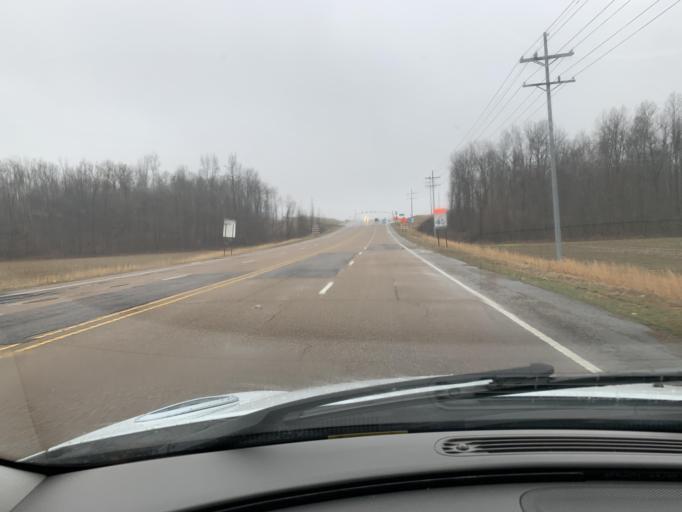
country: US
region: Mississippi
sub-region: De Soto County
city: Hernando
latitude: 34.8693
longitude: -89.9707
